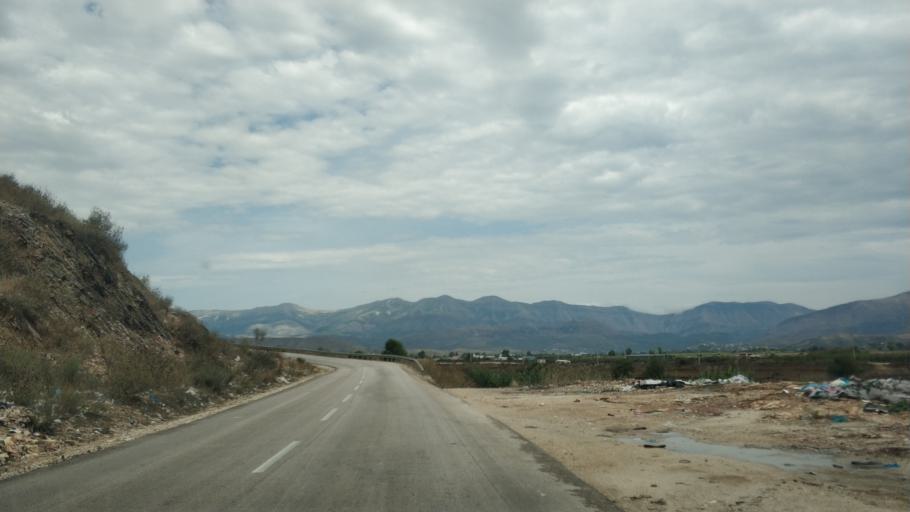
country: AL
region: Vlore
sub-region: Rrethi i Sarandes
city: Sarande
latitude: 39.8555
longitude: 20.0351
